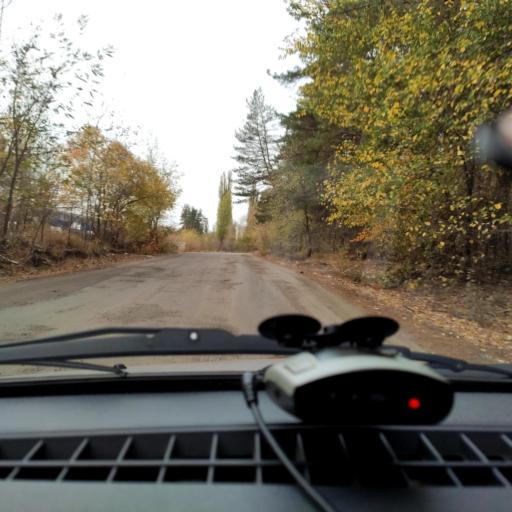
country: RU
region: Voronezj
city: Pridonskoy
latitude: 51.6737
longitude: 39.1229
